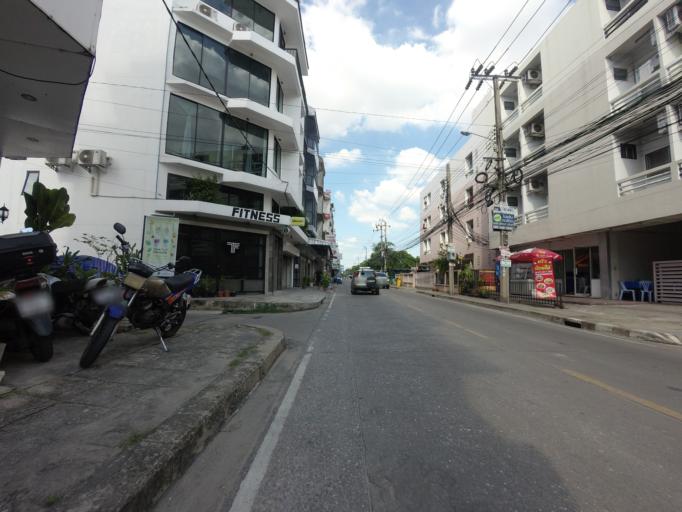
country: TH
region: Bangkok
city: Huai Khwang
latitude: 13.7889
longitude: 100.5913
